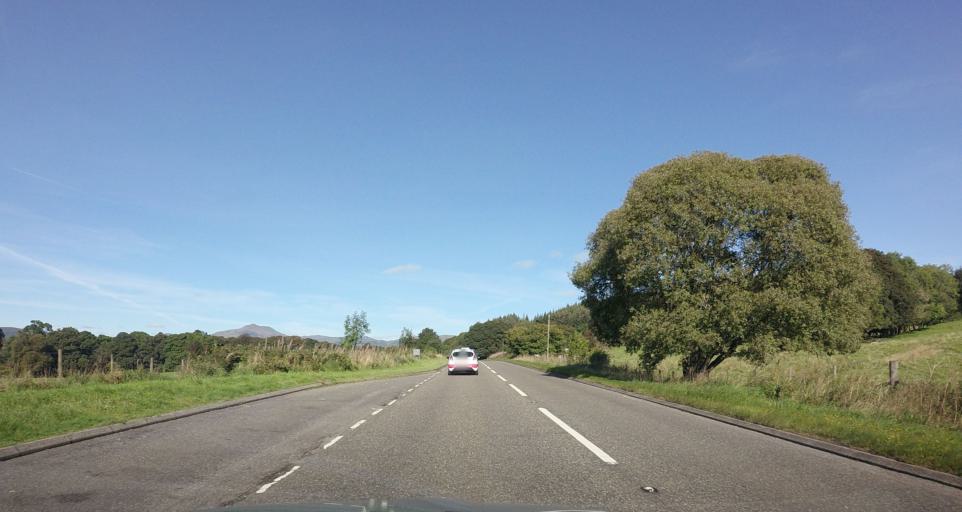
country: GB
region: Scotland
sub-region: Stirling
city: Doune
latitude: 56.2101
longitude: -4.1354
